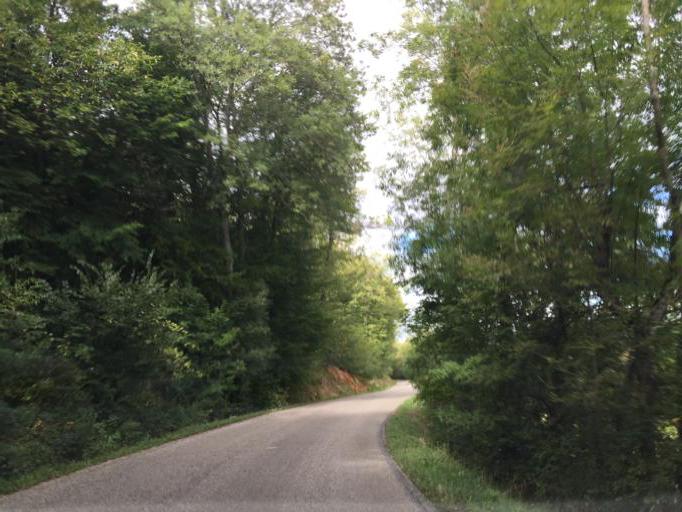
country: FR
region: Rhone-Alpes
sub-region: Departement de la Loire
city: Pelussin
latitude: 45.4644
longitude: 4.6684
